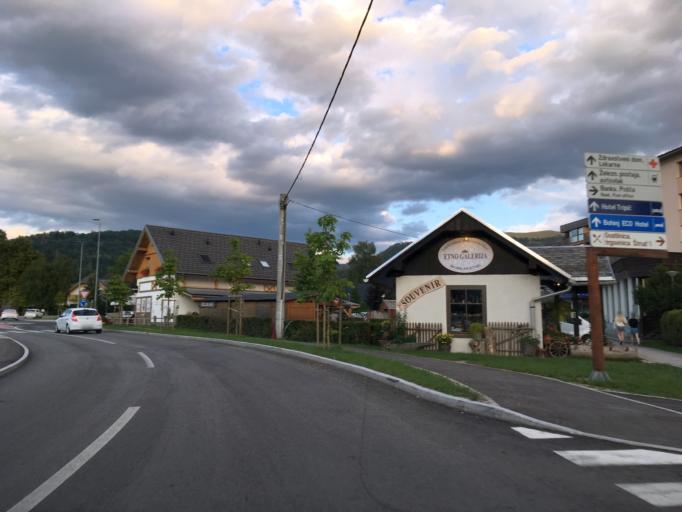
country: SI
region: Bohinj
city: Bohinjska Bistrica
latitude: 46.2726
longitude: 13.9523
